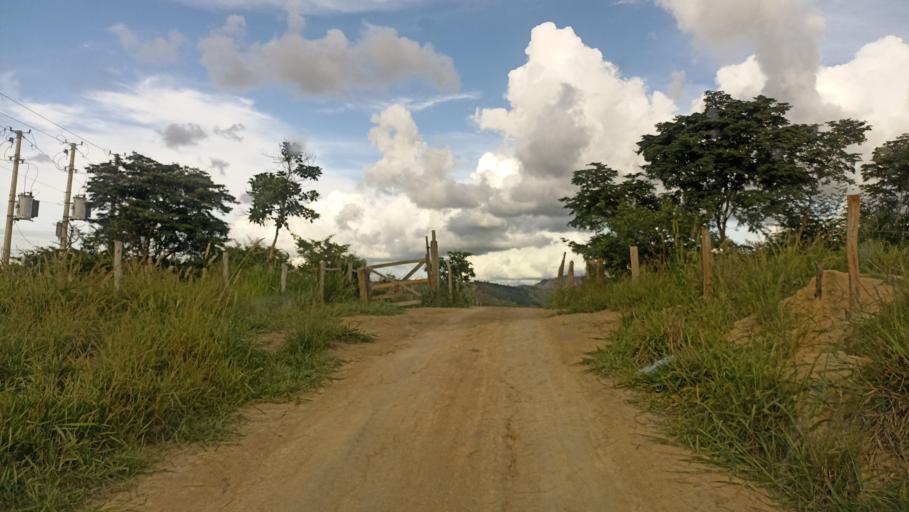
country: BR
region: Minas Gerais
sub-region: Almenara
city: Almenara
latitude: -16.5445
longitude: -40.4492
